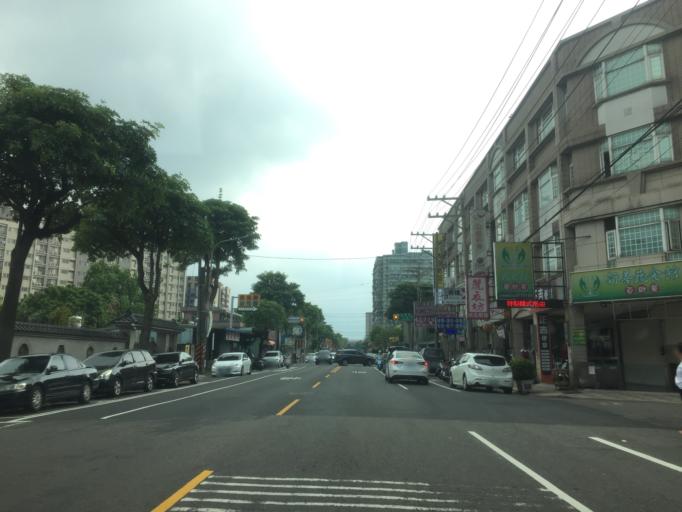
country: TW
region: Taiwan
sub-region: Taoyuan
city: Taoyuan
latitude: 24.9625
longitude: 121.3068
